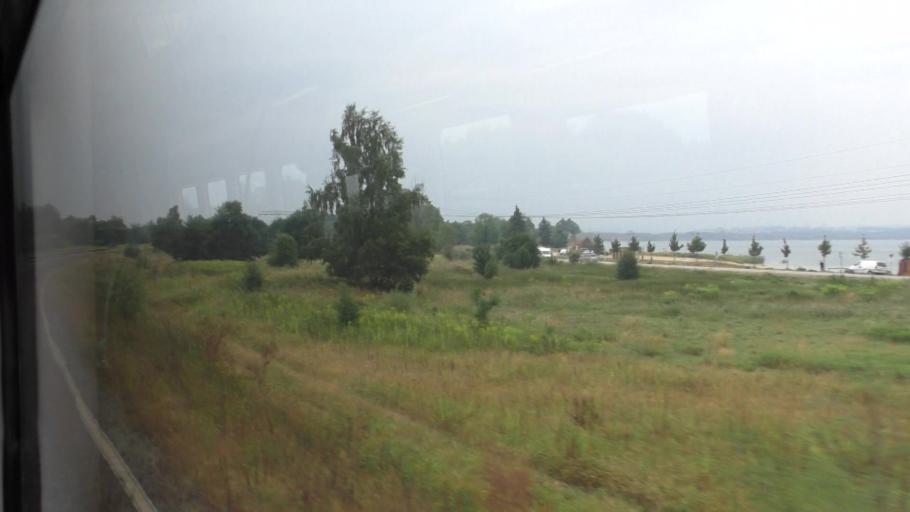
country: DE
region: Saxony
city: Goerlitz
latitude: 51.1047
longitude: 14.9781
